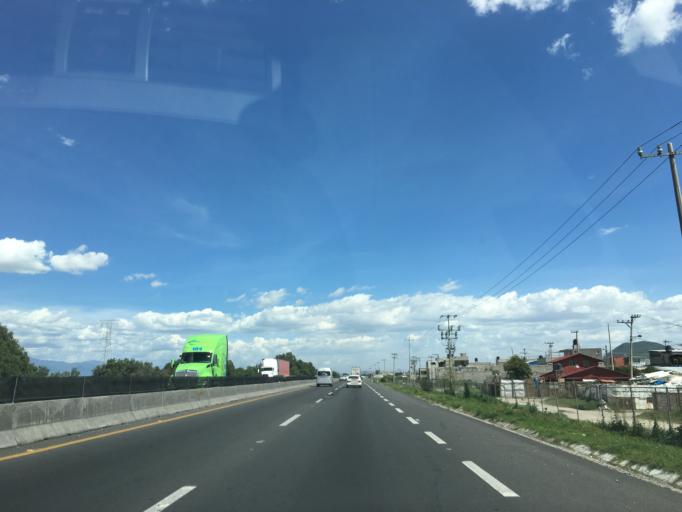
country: MX
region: Mexico
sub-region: Jaltenco
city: Alborada Jaltenco
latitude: 19.6590
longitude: -99.0632
